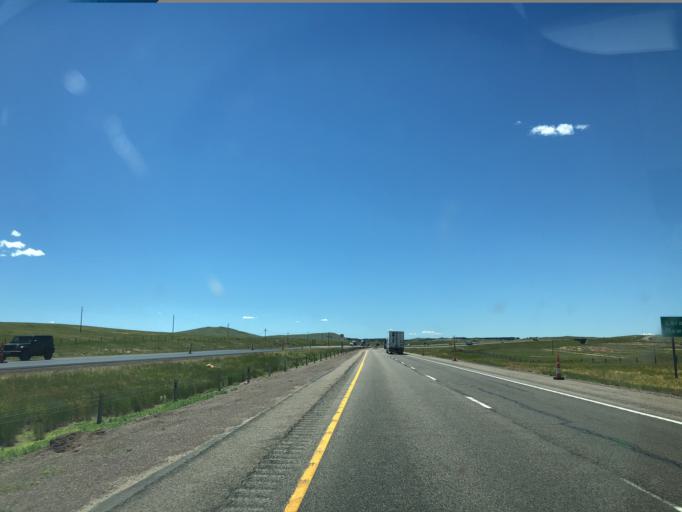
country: US
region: Wyoming
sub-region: Laramie County
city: Cheyenne
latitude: 41.0959
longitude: -105.1942
